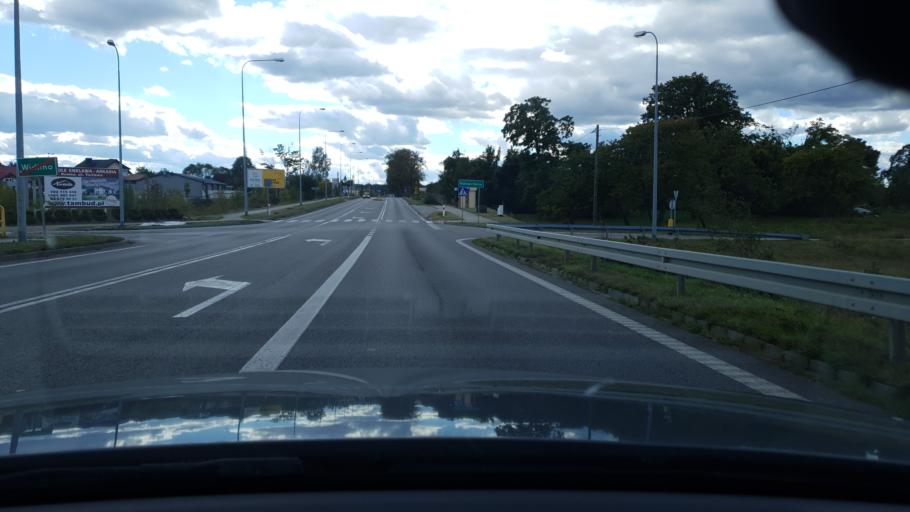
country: PL
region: Pomeranian Voivodeship
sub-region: Powiat wejherowski
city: Rekowo Dolne
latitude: 54.6479
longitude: 18.3547
